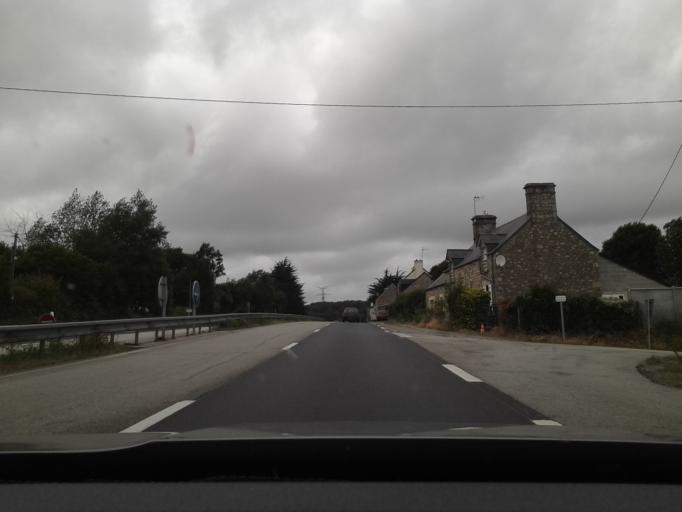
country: FR
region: Lower Normandy
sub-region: Departement de la Manche
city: Brix
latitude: 49.5421
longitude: -1.5479
